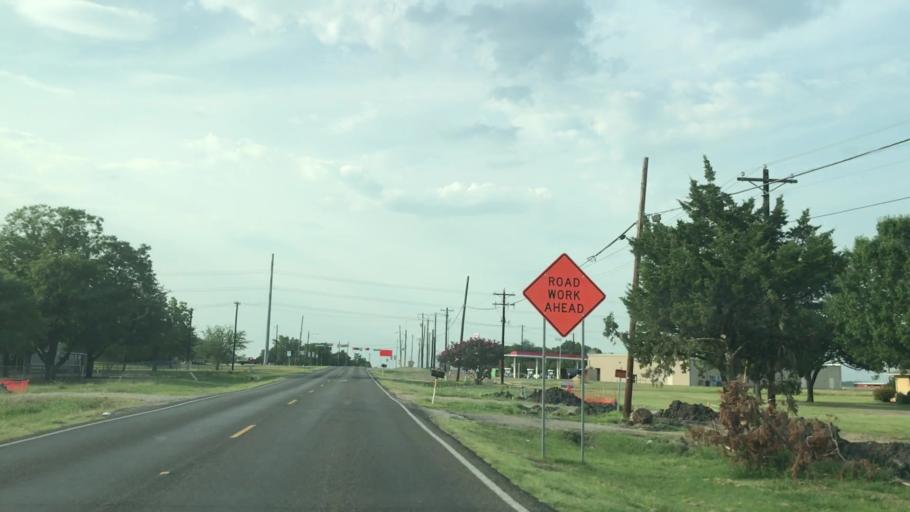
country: US
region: Texas
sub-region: Rockwall County
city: Fate
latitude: 32.9341
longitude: -96.4180
